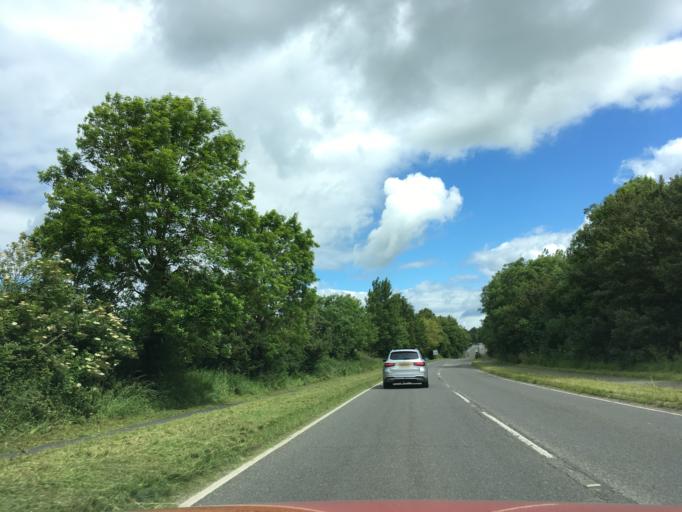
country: GB
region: England
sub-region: Oxfordshire
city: Chipping Norton
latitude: 51.9303
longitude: -1.5417
